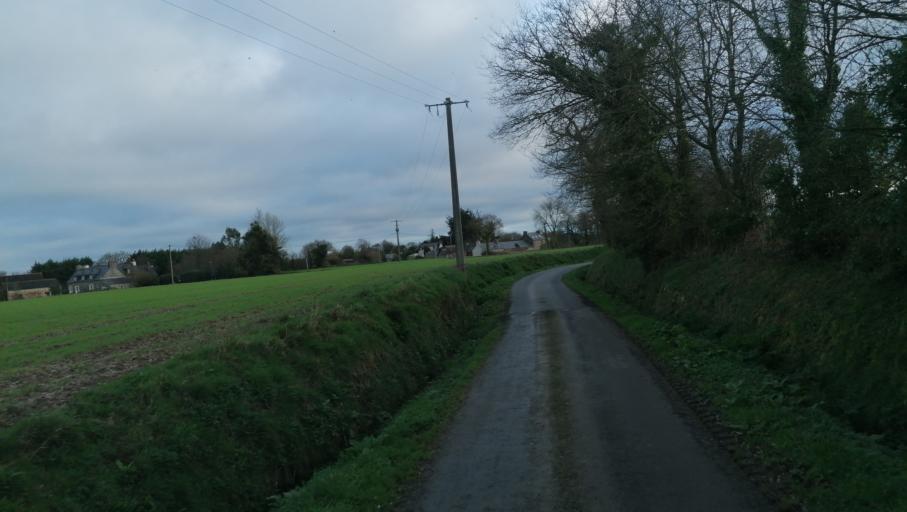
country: FR
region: Brittany
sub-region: Departement des Cotes-d'Armor
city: Pommerit-le-Vicomte
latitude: 48.6436
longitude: -3.0695
